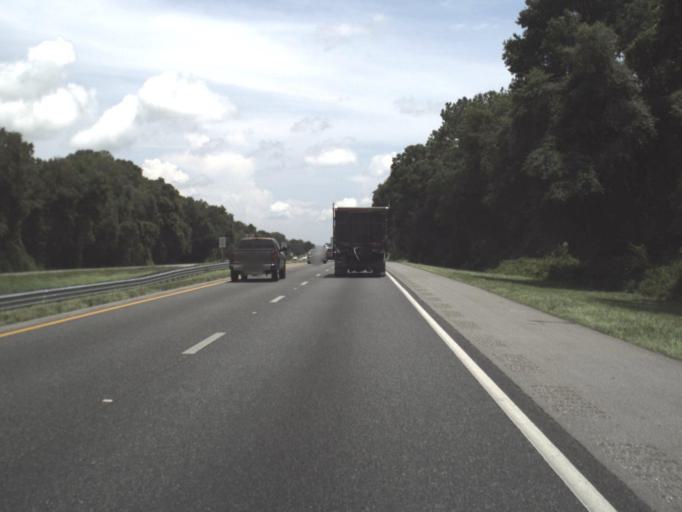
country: US
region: Florida
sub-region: Hernando County
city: Hill 'n Dale
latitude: 28.5670
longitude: -82.2315
